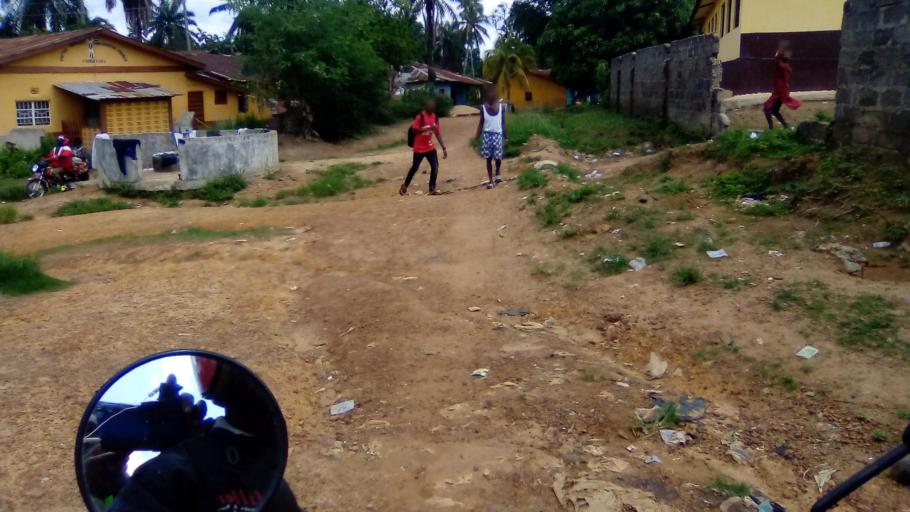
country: SL
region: Southern Province
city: Bo
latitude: 7.9628
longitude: -11.7294
